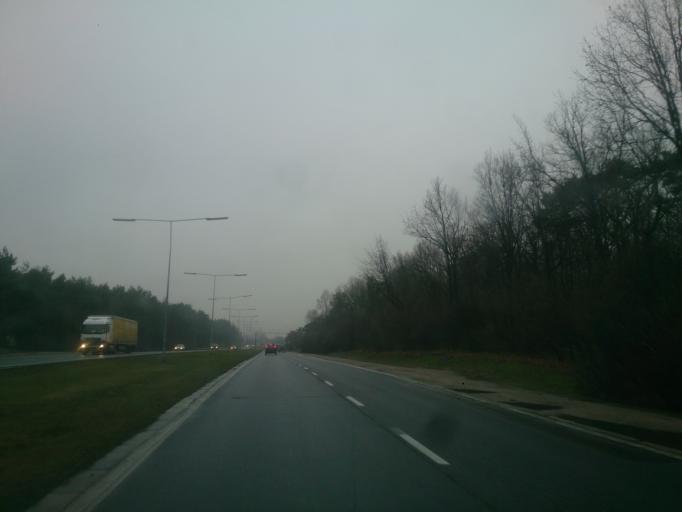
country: PL
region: Masovian Voivodeship
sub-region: Warszawa
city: Bielany
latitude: 52.3191
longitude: 20.9159
